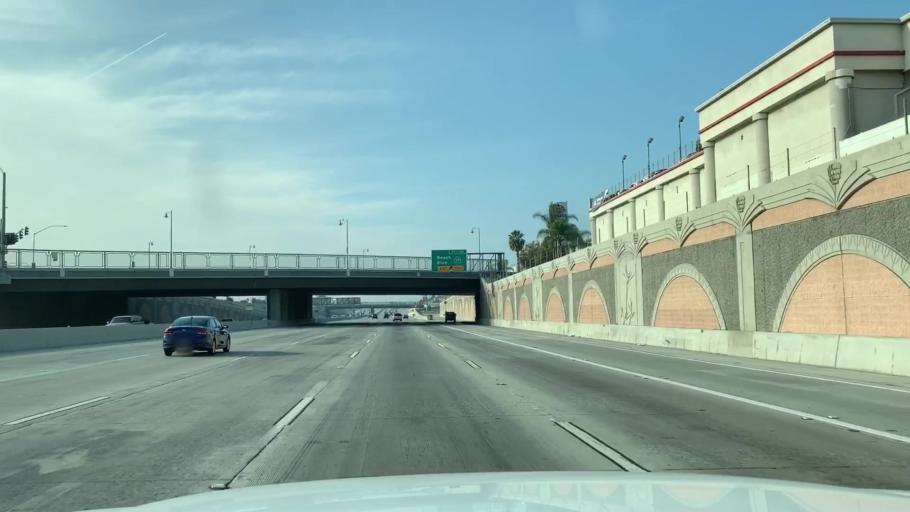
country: US
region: California
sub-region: Orange County
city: Buena Park
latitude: 33.8659
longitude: -117.9970
